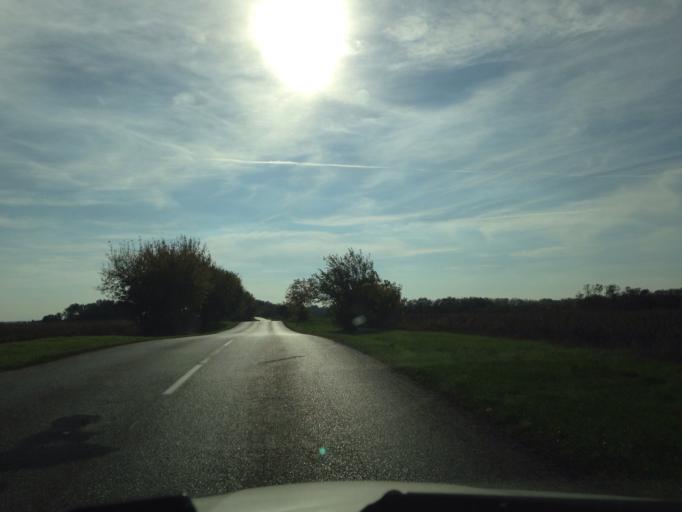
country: SK
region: Nitriansky
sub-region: Okres Komarno
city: Hurbanovo
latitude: 47.8214
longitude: 18.2289
